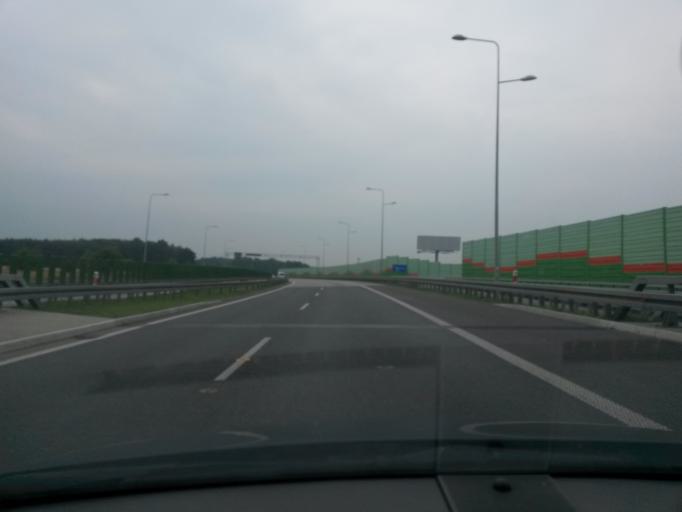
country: PL
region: Lodz Voivodeship
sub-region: Powiat piotrkowski
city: Wolborz
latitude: 51.4931
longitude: 19.8329
